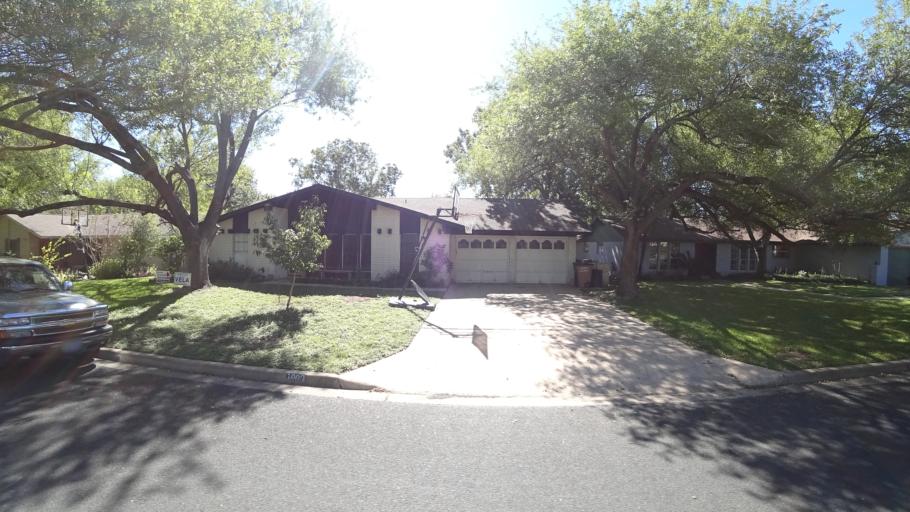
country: US
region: Texas
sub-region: Travis County
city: Austin
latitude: 30.3045
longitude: -97.6925
